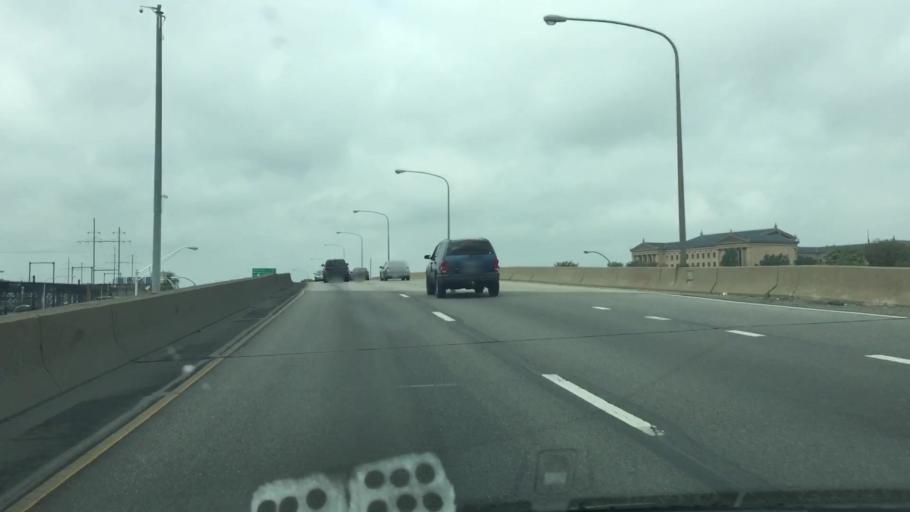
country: US
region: Pennsylvania
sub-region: Philadelphia County
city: Philadelphia
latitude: 39.9600
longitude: -75.1811
